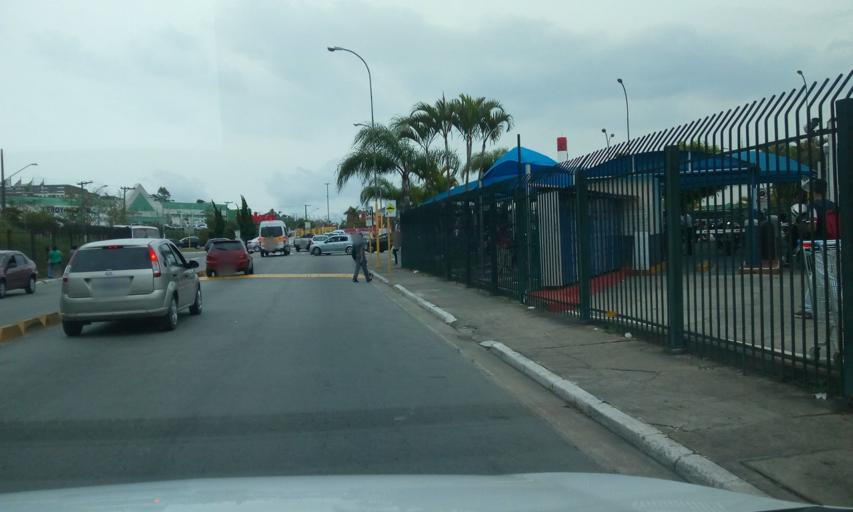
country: BR
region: Sao Paulo
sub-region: Diadema
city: Diadema
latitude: -23.6772
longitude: -46.6737
